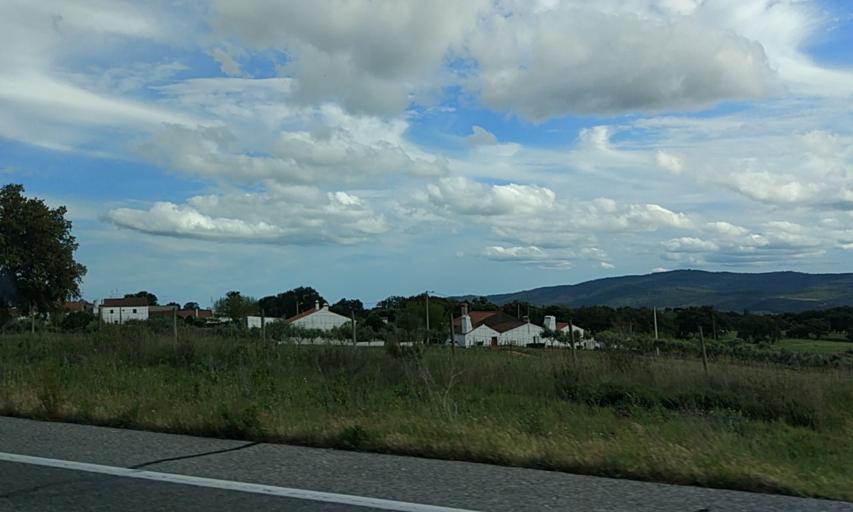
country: PT
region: Evora
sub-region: Estremoz
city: Estremoz
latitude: 38.8098
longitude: -7.5422
